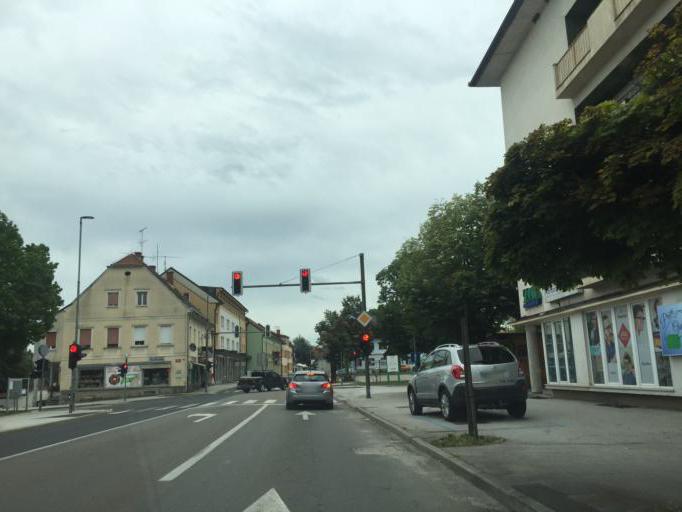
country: SI
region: Gornja Radgona
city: Gornja Radgona
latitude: 46.6770
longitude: 15.9906
